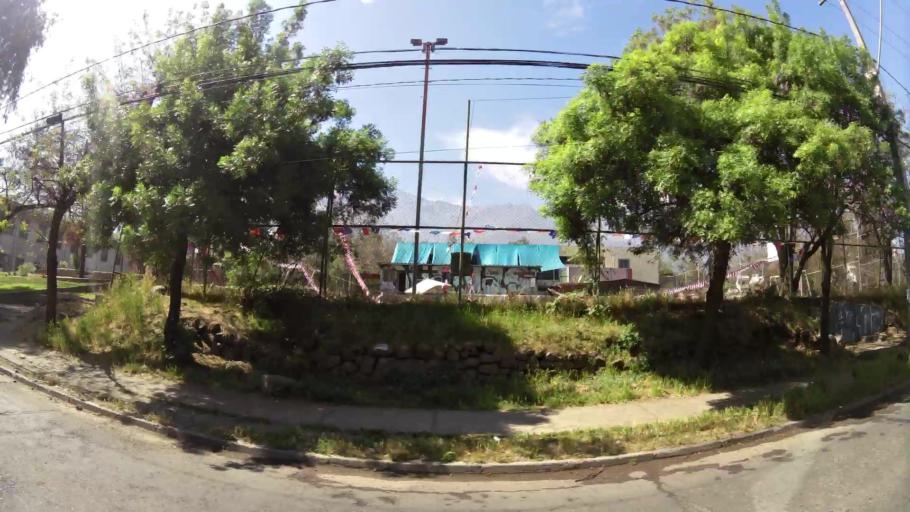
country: CL
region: Santiago Metropolitan
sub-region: Provincia de Santiago
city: Villa Presidente Frei, Nunoa, Santiago, Chile
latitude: -33.4709
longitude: -70.5327
